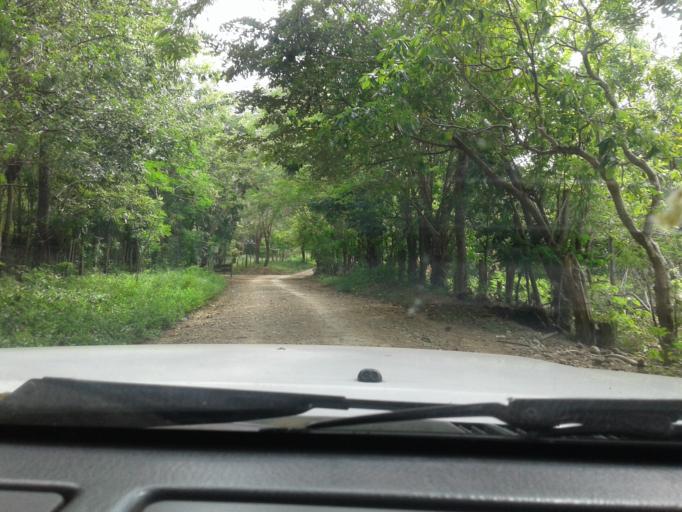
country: NI
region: Rivas
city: San Juan del Sur
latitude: 11.2122
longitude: -85.7970
